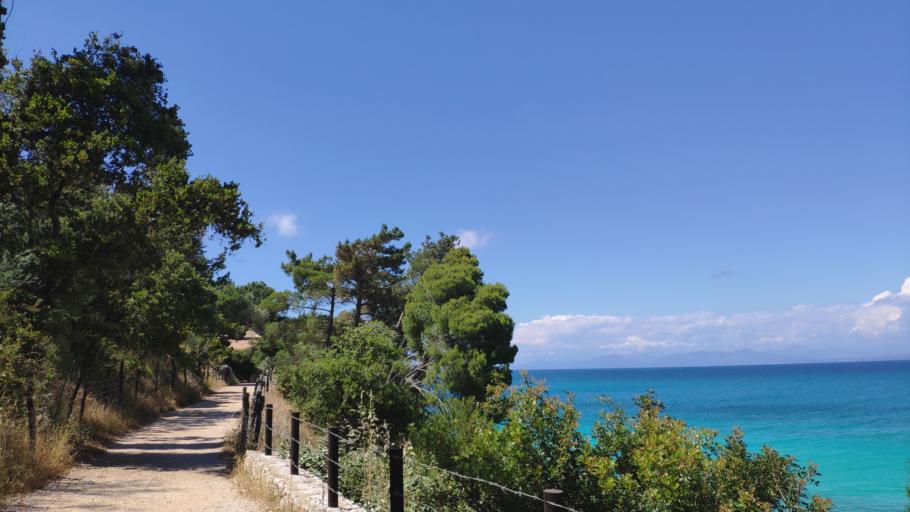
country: GR
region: Ionian Islands
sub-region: Lefkada
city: Lefkada
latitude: 38.8318
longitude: 20.6666
